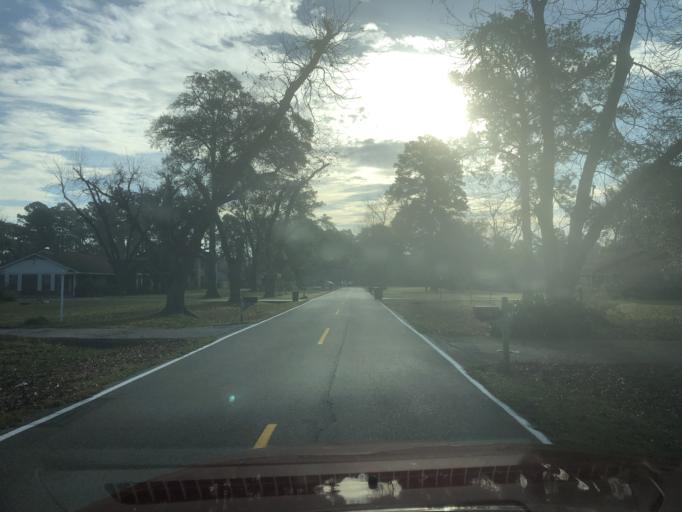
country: US
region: Texas
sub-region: Harris County
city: Spring
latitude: 30.0113
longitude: -95.4704
